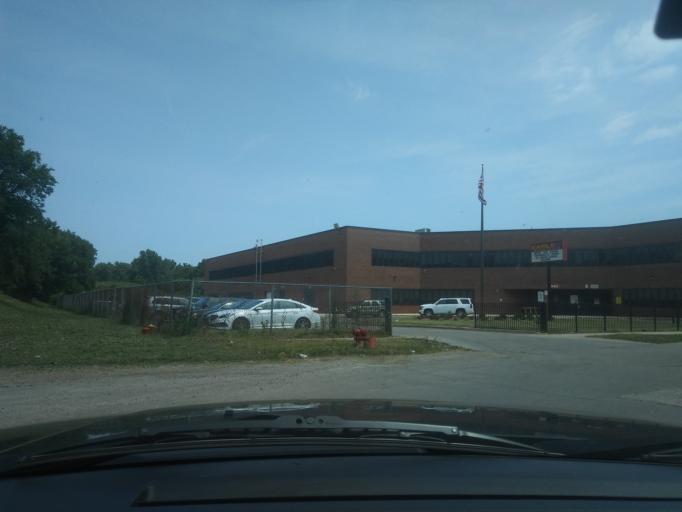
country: US
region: Illinois
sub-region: Cook County
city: Evergreen Park
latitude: 41.7811
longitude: -87.6763
